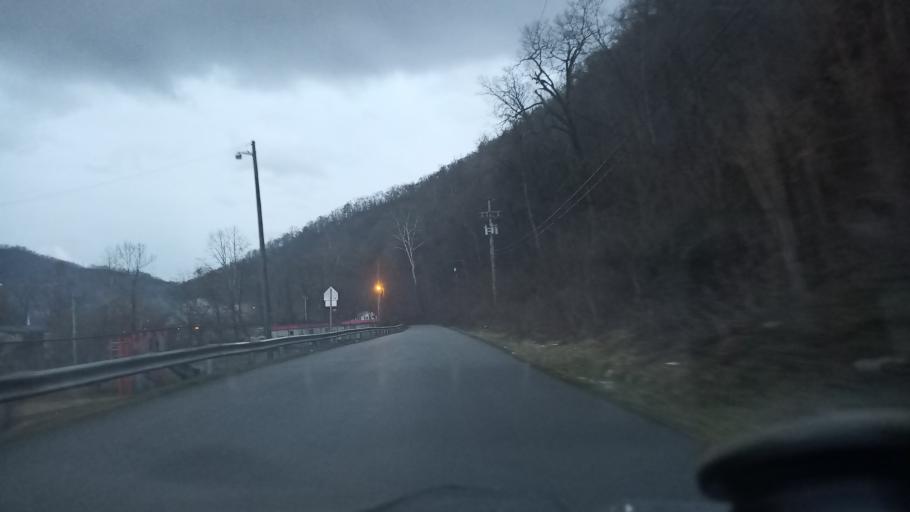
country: US
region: West Virginia
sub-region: Logan County
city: Mallory
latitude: 37.7287
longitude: -81.8775
